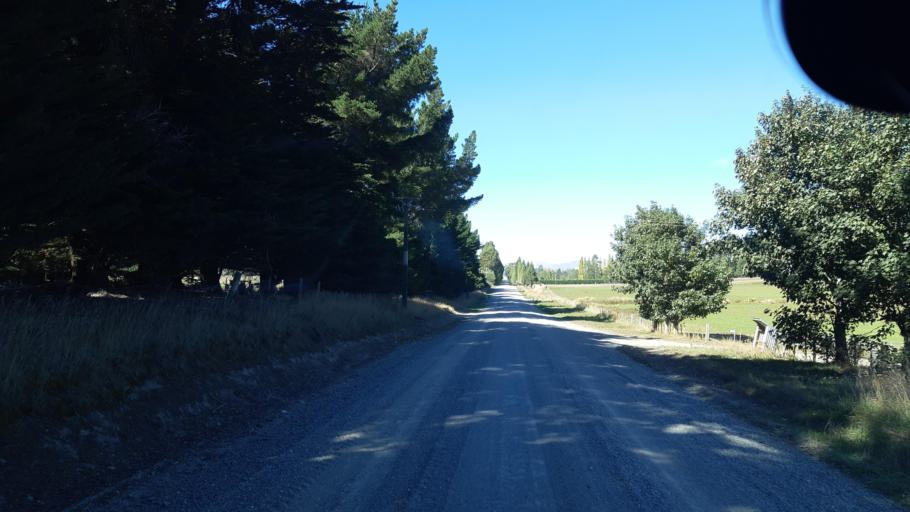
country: NZ
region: Southland
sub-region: Southland District
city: Winton
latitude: -45.8821
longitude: 168.5144
